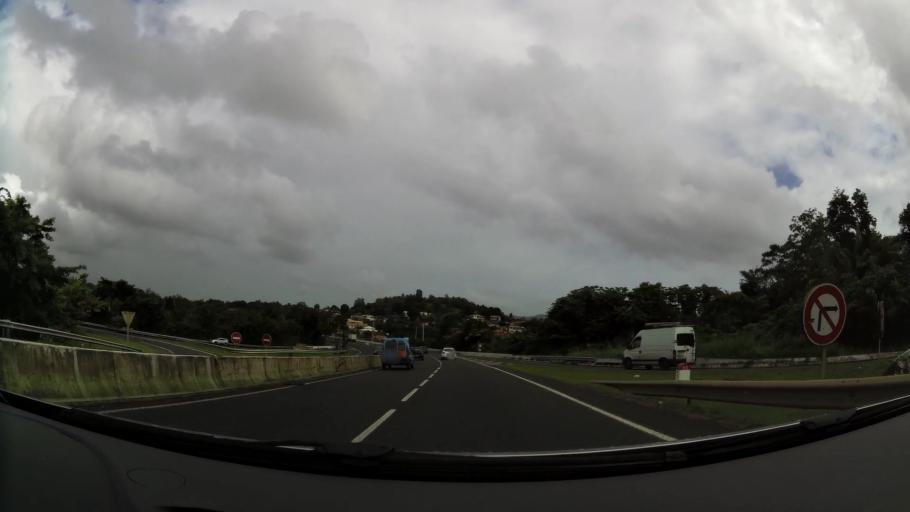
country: MQ
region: Martinique
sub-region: Martinique
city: Ducos
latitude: 14.5816
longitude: -60.9801
